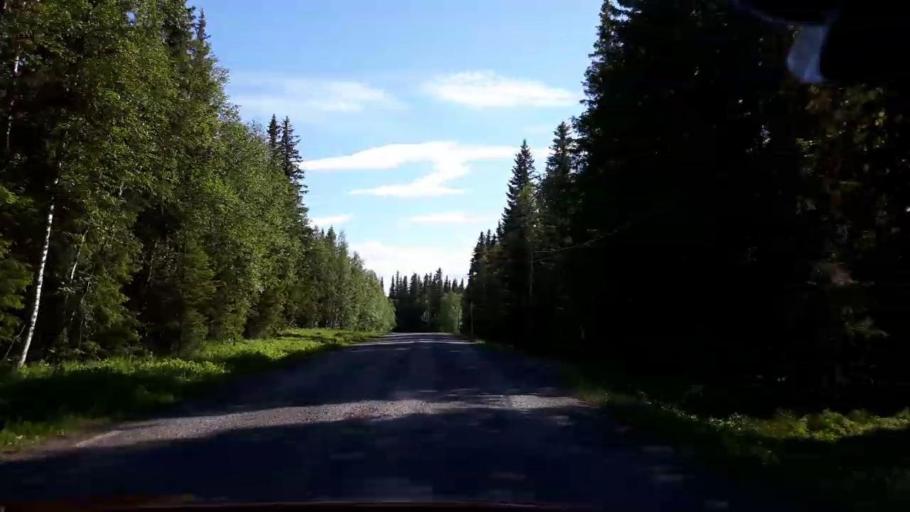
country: SE
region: Jaemtland
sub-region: Krokoms Kommun
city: Valla
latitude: 63.7354
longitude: 14.1189
